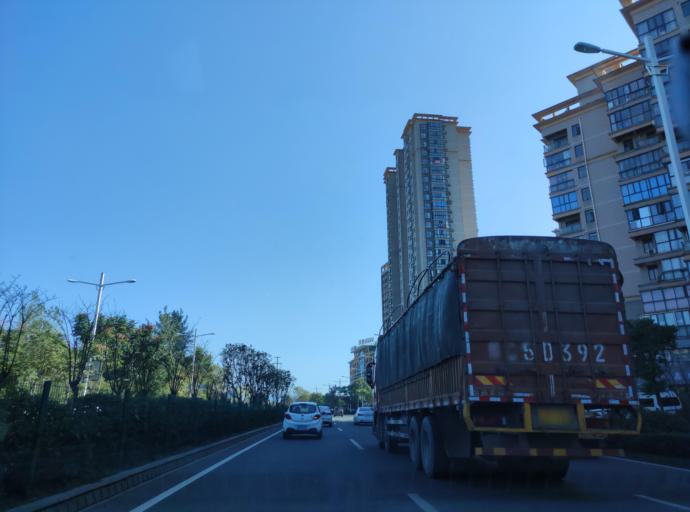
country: CN
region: Jiangxi Sheng
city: Pingxiang
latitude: 27.6592
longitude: 113.8471
